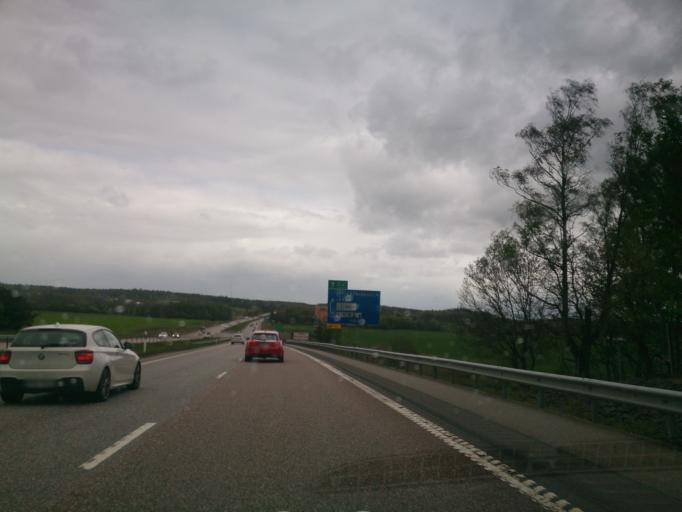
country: SE
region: Stockholm
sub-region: Sodertalje Kommun
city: Pershagen
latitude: 59.0741
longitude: 17.5928
